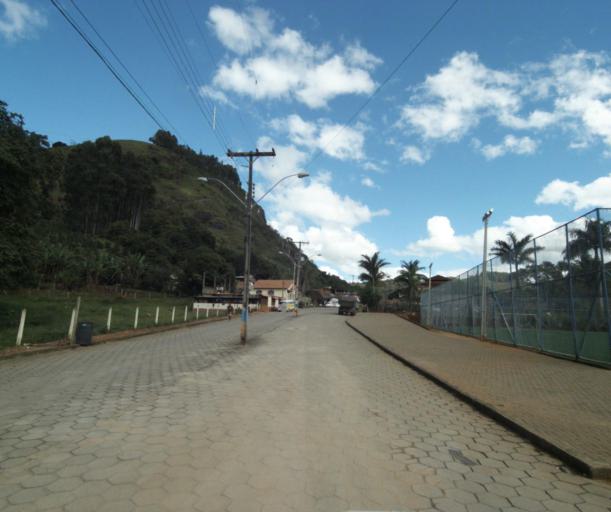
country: BR
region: Espirito Santo
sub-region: Irupi
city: Irupi
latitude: -20.5310
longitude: -41.6671
